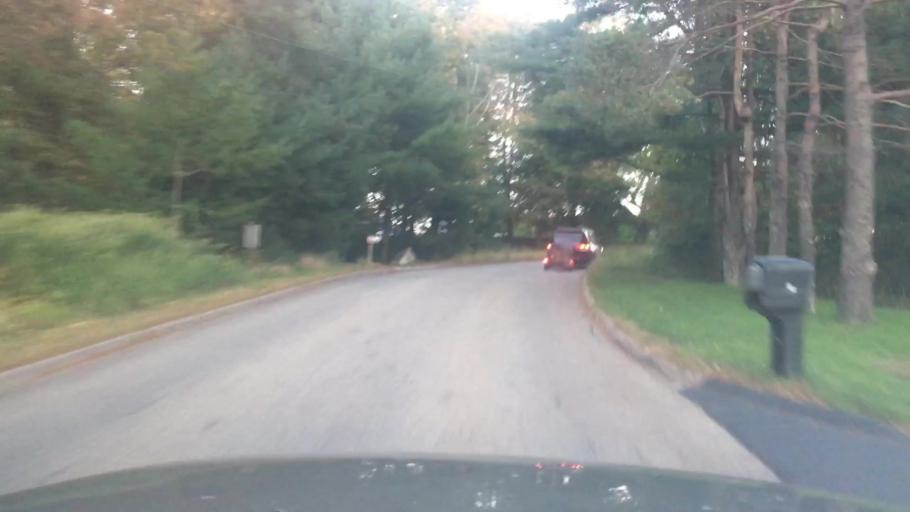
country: US
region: Massachusetts
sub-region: Worcester County
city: Charlton
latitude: 42.1322
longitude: -71.9732
